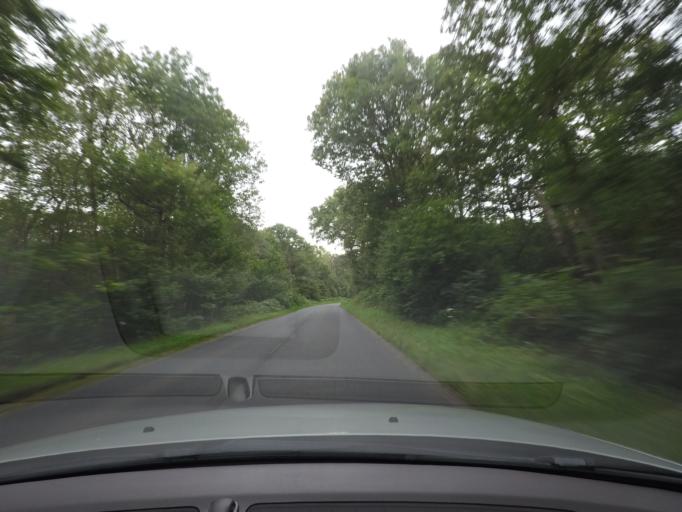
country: FR
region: Haute-Normandie
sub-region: Departement de la Seine-Maritime
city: Ymare
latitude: 49.3371
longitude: 1.1927
